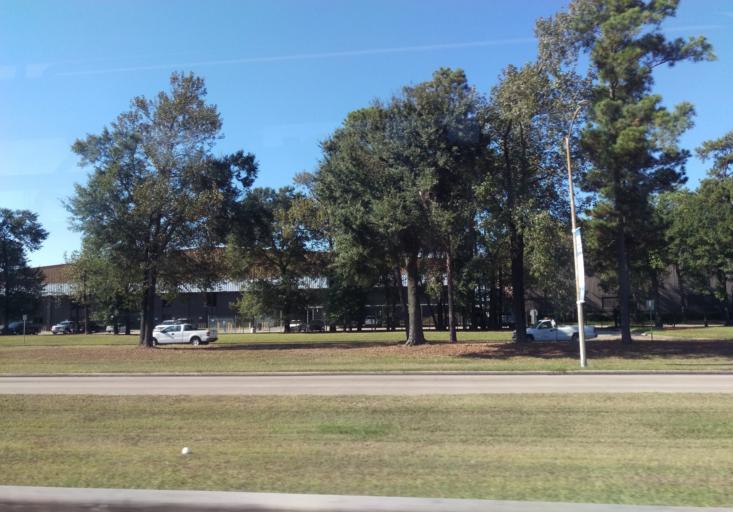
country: US
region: Texas
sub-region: Harris County
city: Aldine
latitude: 29.9721
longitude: -95.3402
